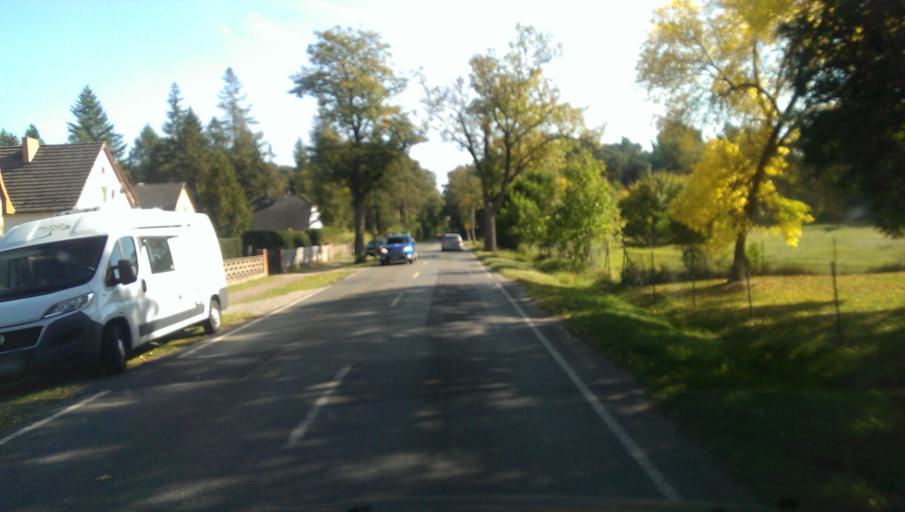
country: DE
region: Brandenburg
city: Teupitz
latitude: 52.1305
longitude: 13.6231
